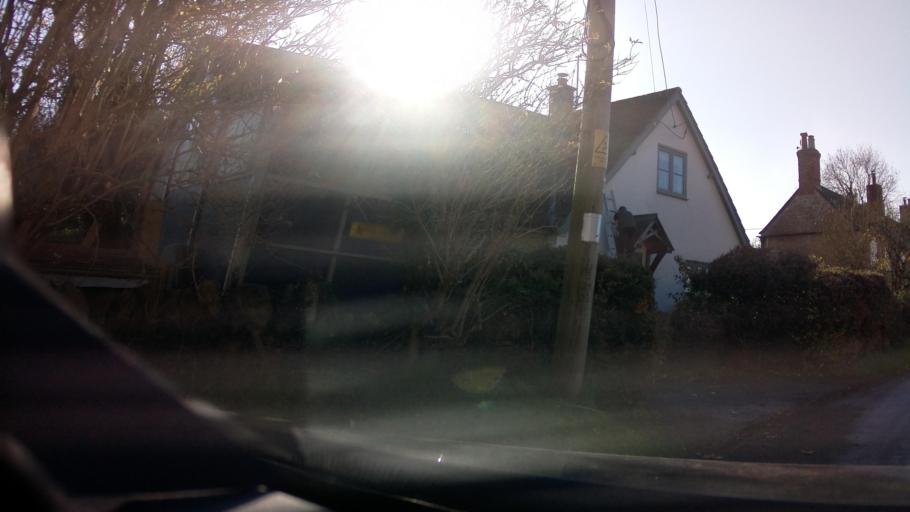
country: GB
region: England
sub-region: Somerset
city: Bruton
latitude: 51.0809
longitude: -2.4663
